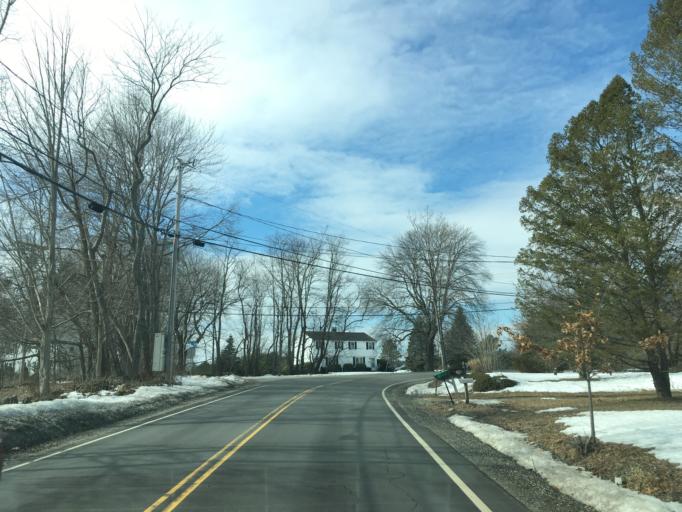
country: US
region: New Hampshire
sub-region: Rockingham County
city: North Hampton
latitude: 42.9919
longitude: -70.8838
